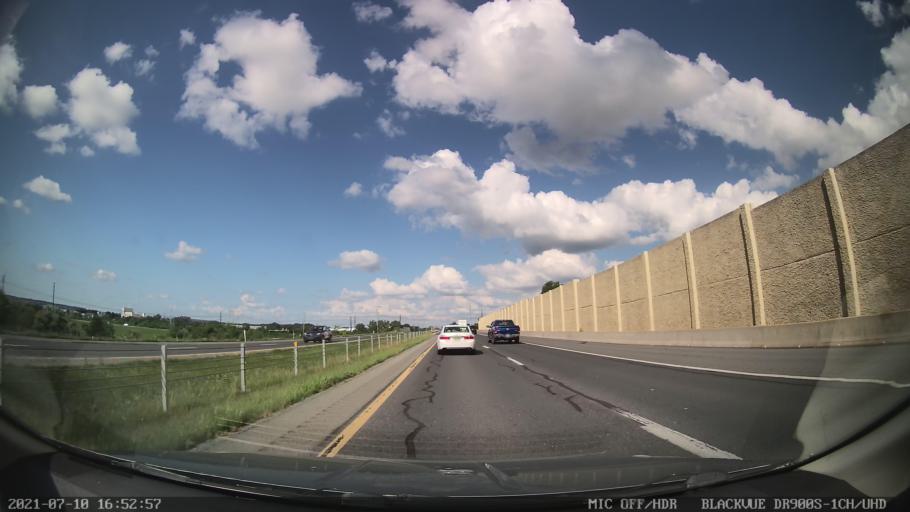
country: US
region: Pennsylvania
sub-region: Lehigh County
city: Trexlertown
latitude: 40.5575
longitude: -75.6111
